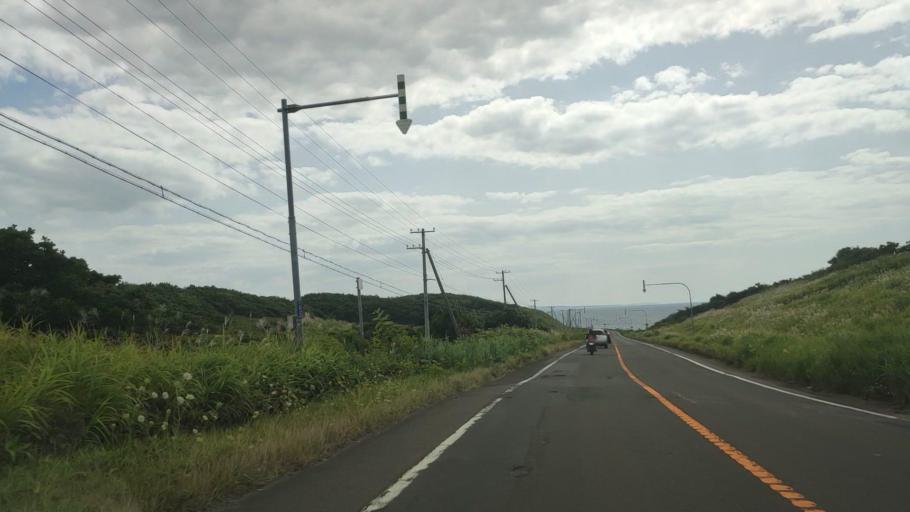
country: JP
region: Hokkaido
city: Rumoi
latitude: 44.5122
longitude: 141.7662
